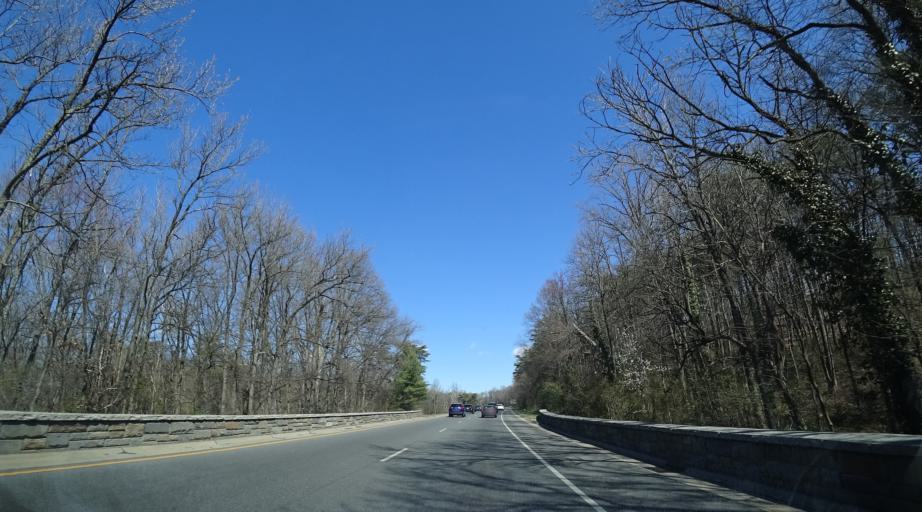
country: US
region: Maryland
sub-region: Prince George's County
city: East Riverdale
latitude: 38.9541
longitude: -76.9080
